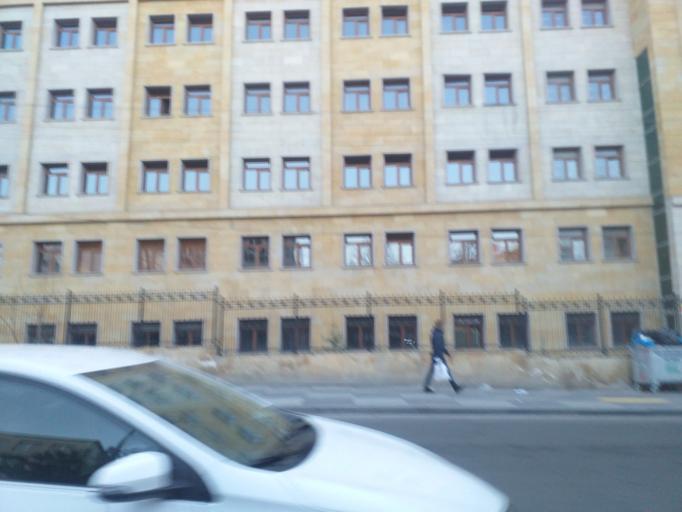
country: TR
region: Ankara
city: Ankara
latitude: 39.9431
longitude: 32.8247
